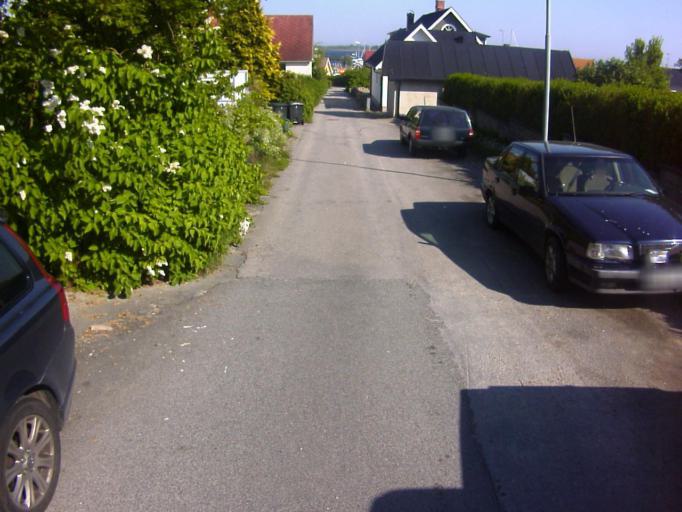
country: SE
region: Blekinge
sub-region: Solvesborgs Kommun
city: Soelvesborg
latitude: 56.0106
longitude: 14.6936
